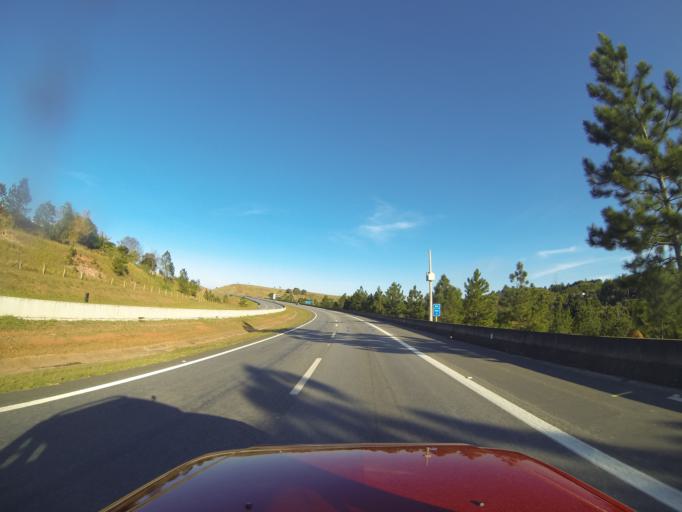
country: BR
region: Sao Paulo
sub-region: Jacarei
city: Jacarei
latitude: -23.3161
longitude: -46.0450
